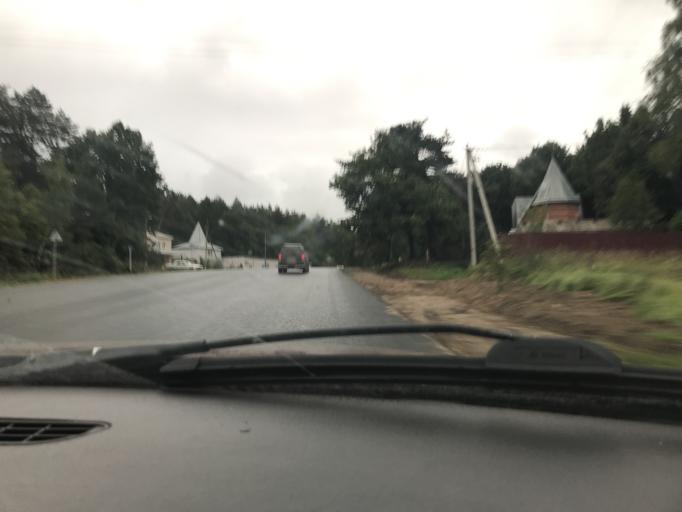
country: RU
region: Kaluga
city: Kurovskoye
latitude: 54.6056
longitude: 36.0463
